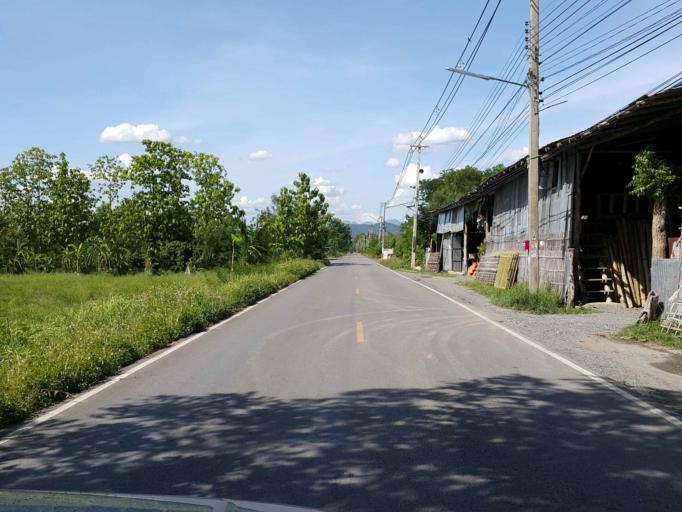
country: TH
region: Chiang Mai
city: San Kamphaeng
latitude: 18.7650
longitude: 99.1457
